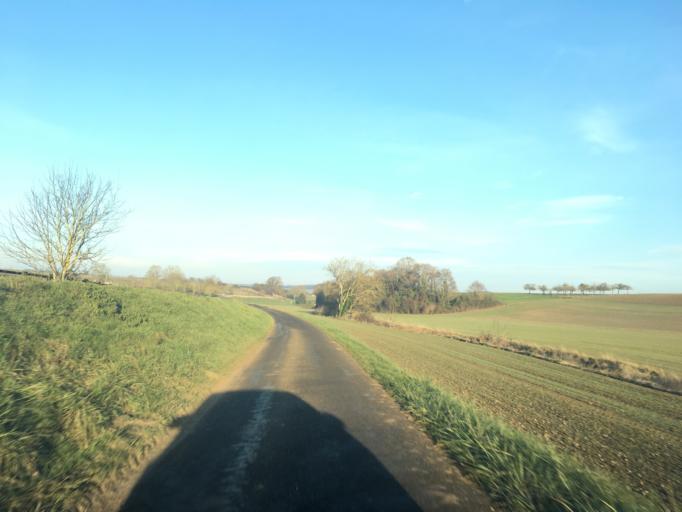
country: FR
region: Haute-Normandie
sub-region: Departement de l'Eure
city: Menilles
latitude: 49.0490
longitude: 1.2920
